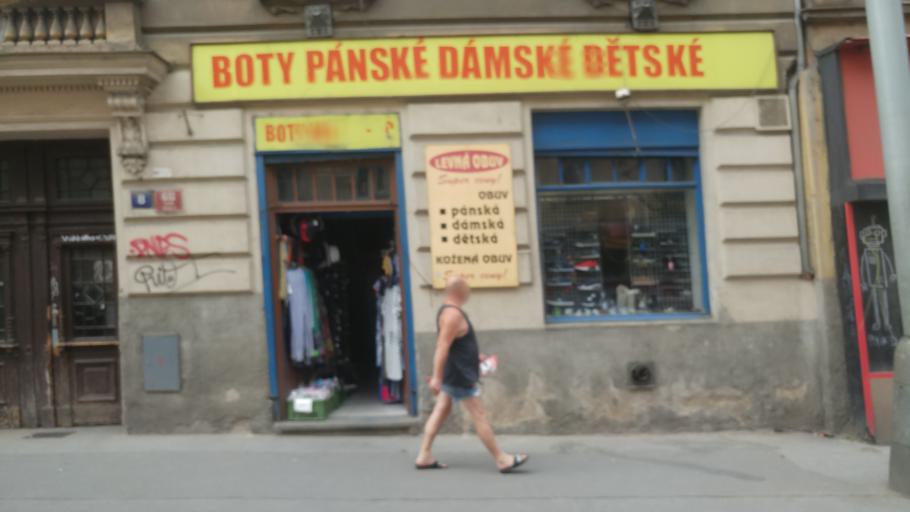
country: CZ
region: Praha
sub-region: Praha 8
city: Karlin
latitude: 50.0835
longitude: 14.4541
